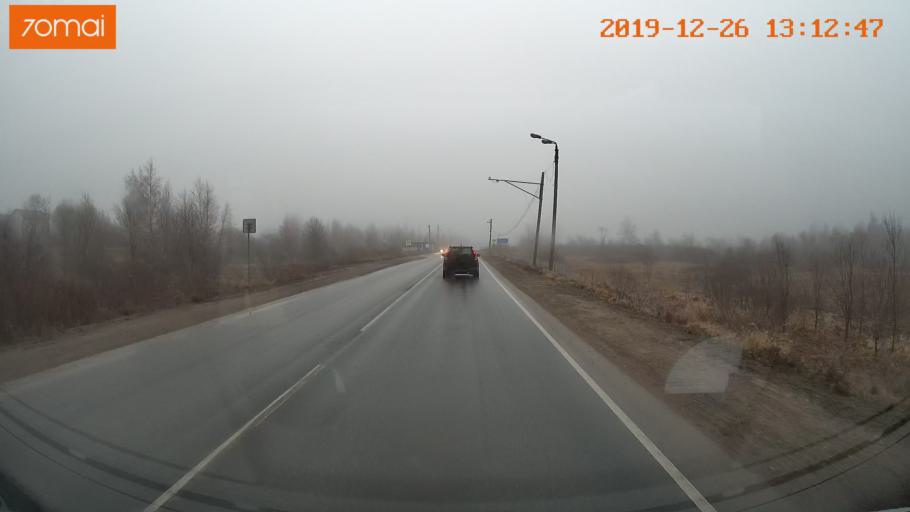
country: RU
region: Vologda
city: Cherepovets
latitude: 59.0215
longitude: 38.0411
